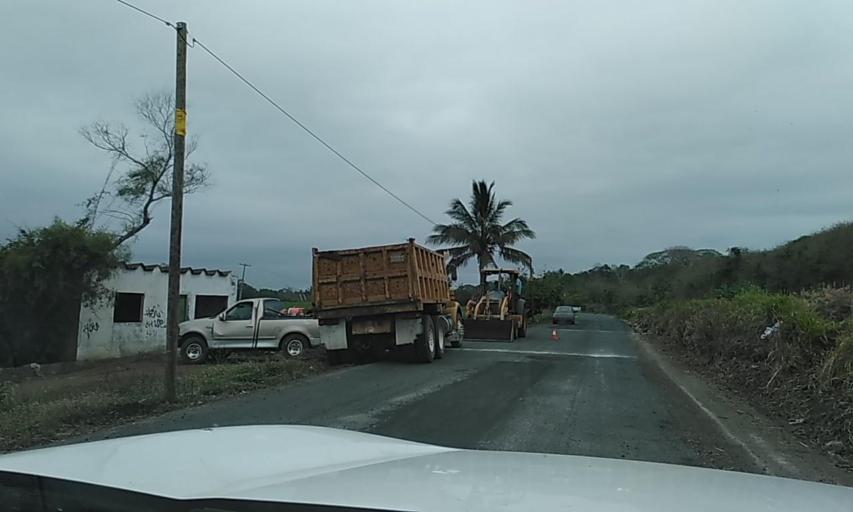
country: MX
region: Veracruz
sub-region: La Antigua
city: Nicolas Blanco (San Pancho)
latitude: 19.3094
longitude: -96.3179
